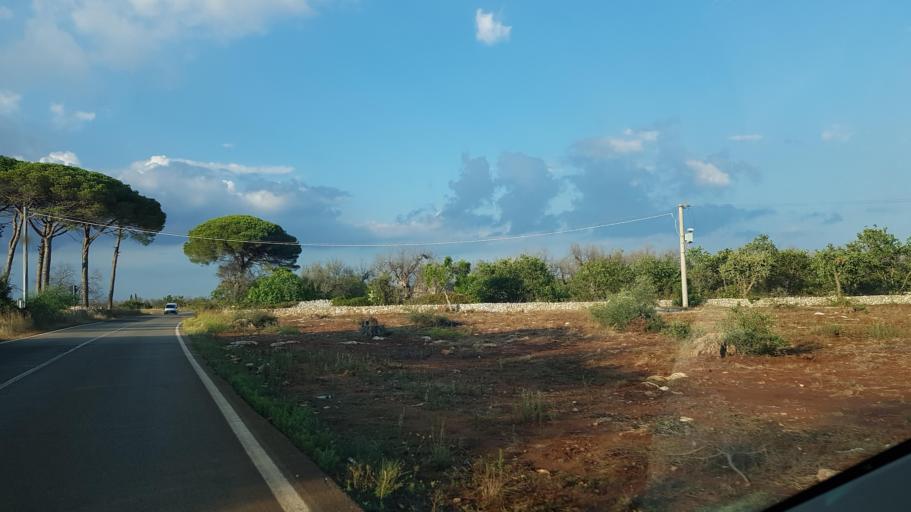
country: IT
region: Apulia
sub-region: Provincia di Lecce
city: Acquarica del Capo
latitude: 39.8840
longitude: 18.2359
